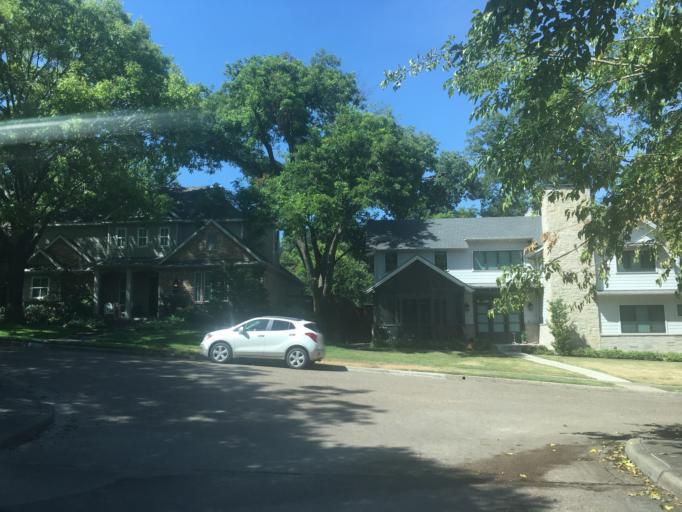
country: US
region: Texas
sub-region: Dallas County
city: Richardson
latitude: 32.8735
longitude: -96.7217
